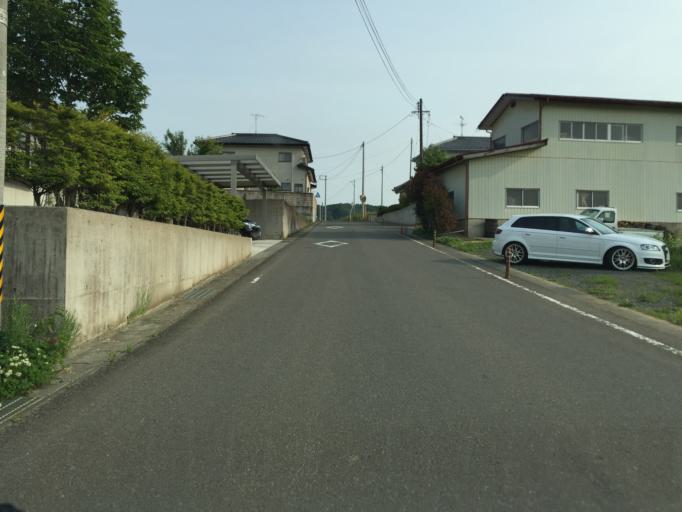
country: JP
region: Fukushima
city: Fukushima-shi
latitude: 37.7112
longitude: 140.4299
